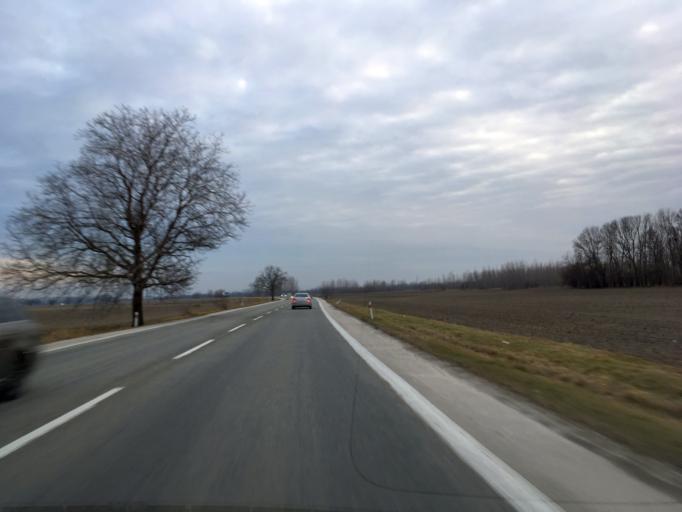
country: SK
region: Trnavsky
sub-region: Okres Dunajska Streda
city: Velky Meder
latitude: 47.9309
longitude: 17.7238
